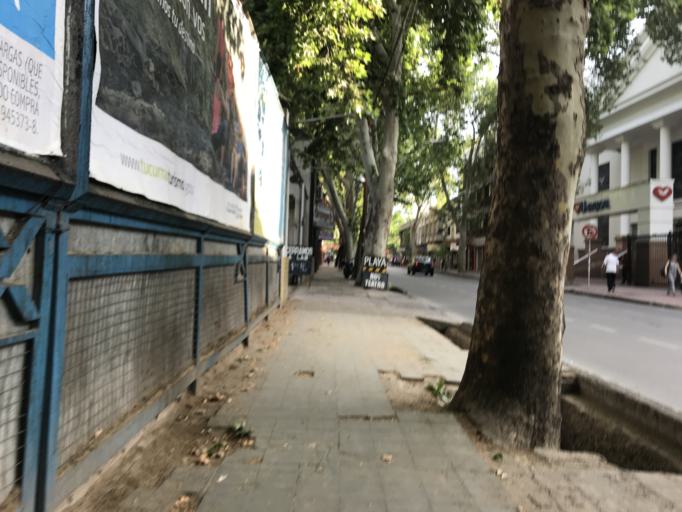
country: AR
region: Mendoza
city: Mendoza
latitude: -32.8864
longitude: -68.8354
